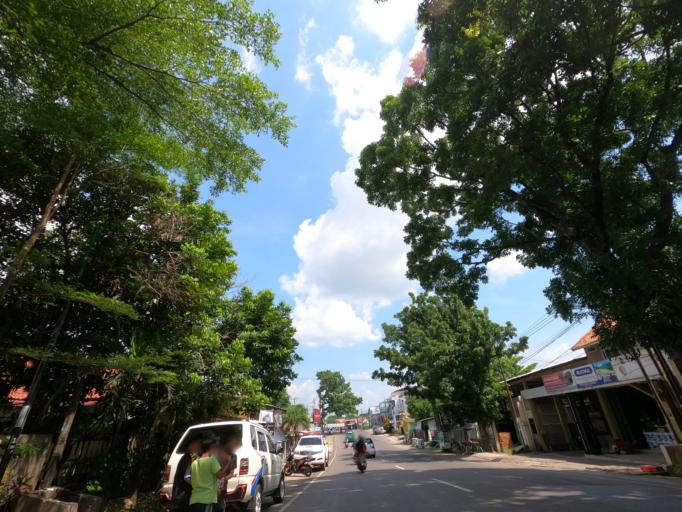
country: ID
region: West Java
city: Pamanukan
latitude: -6.5531
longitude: 107.7549
